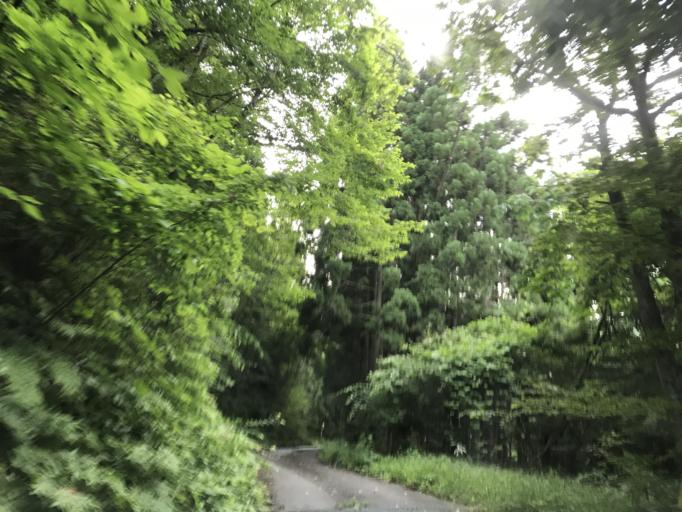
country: JP
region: Iwate
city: Ichinoseki
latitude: 38.9007
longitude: 141.0116
